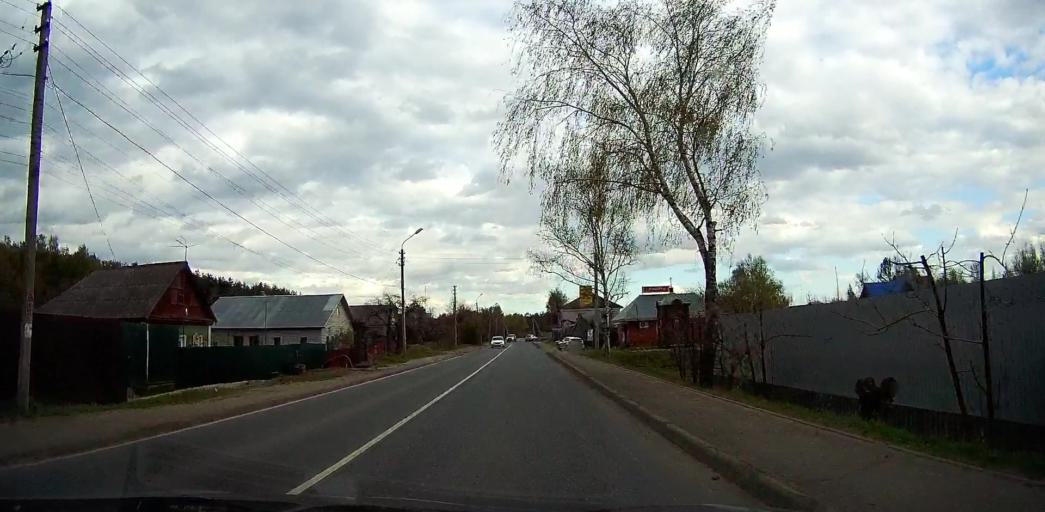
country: RU
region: Moskovskaya
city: Pavlovskiy Posad
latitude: 55.8008
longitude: 38.6840
